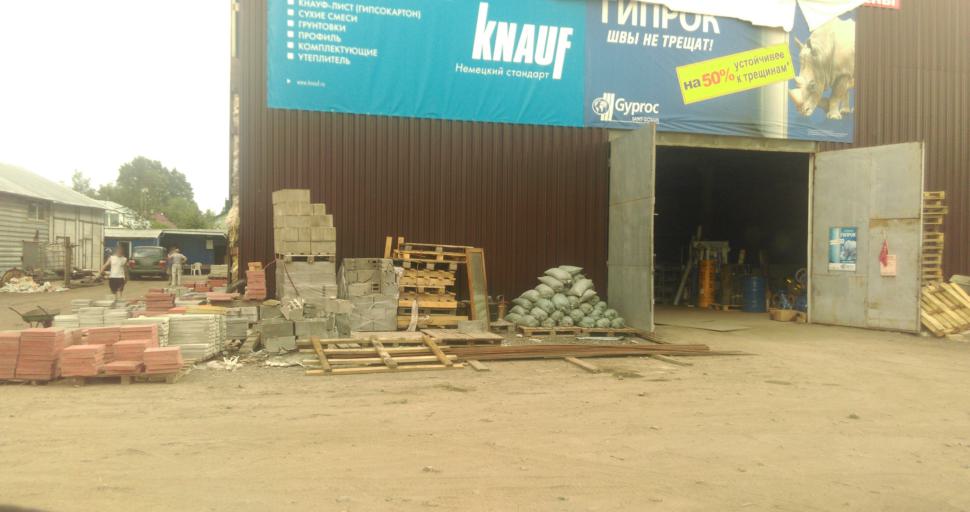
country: RU
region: Moskovskaya
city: Vostryakovo
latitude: 55.3969
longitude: 37.8098
